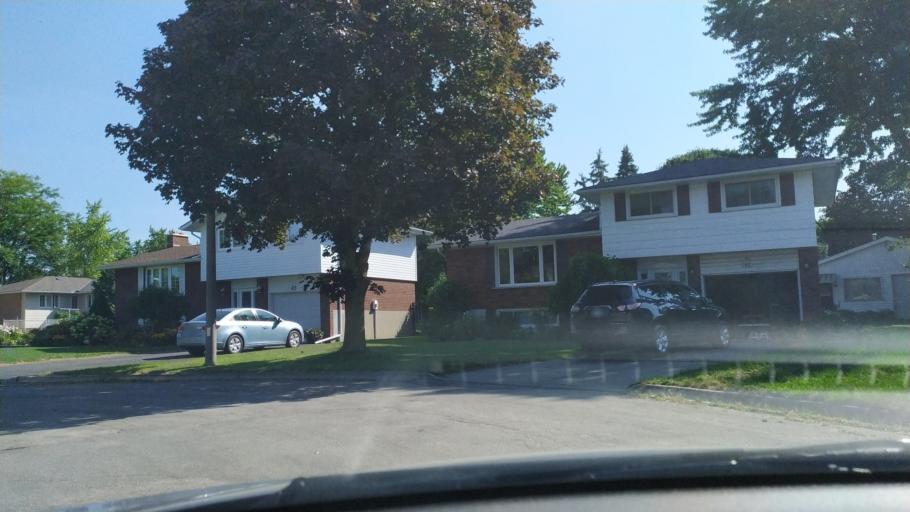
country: CA
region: Ontario
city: Stratford
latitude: 43.3845
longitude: -80.9688
